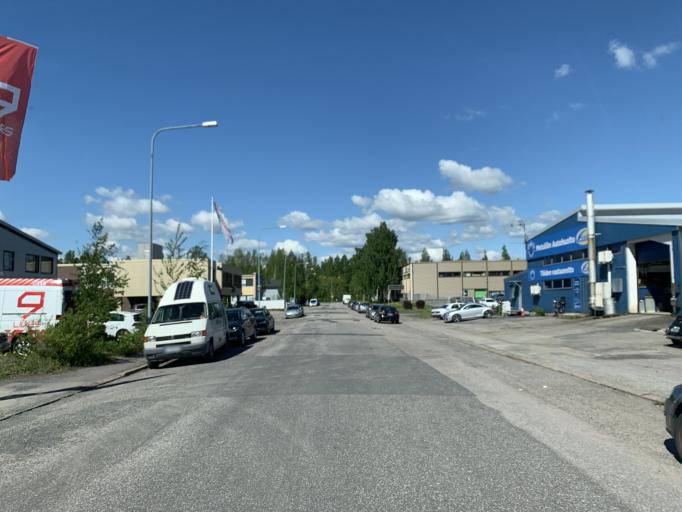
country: FI
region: Uusimaa
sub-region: Helsinki
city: Vantaa
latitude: 60.2545
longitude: 25.0266
